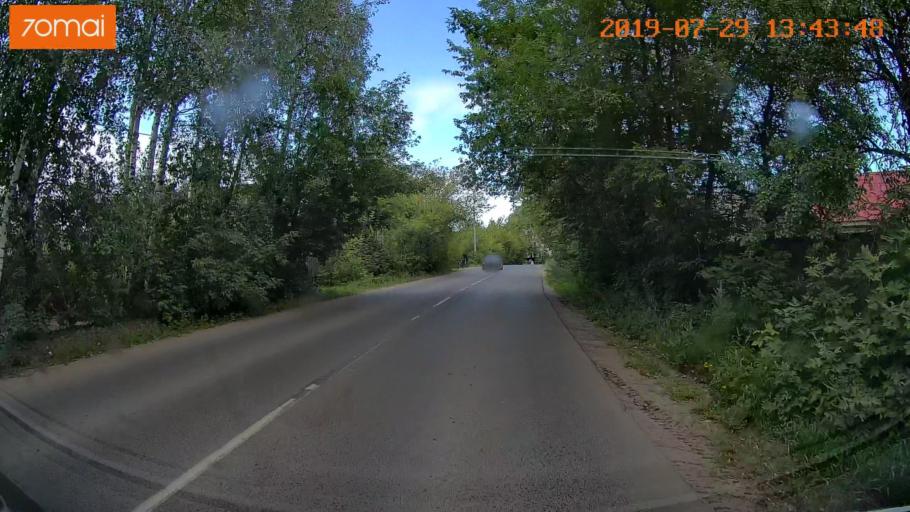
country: RU
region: Ivanovo
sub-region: Gorod Ivanovo
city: Ivanovo
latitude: 57.0066
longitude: 40.9298
